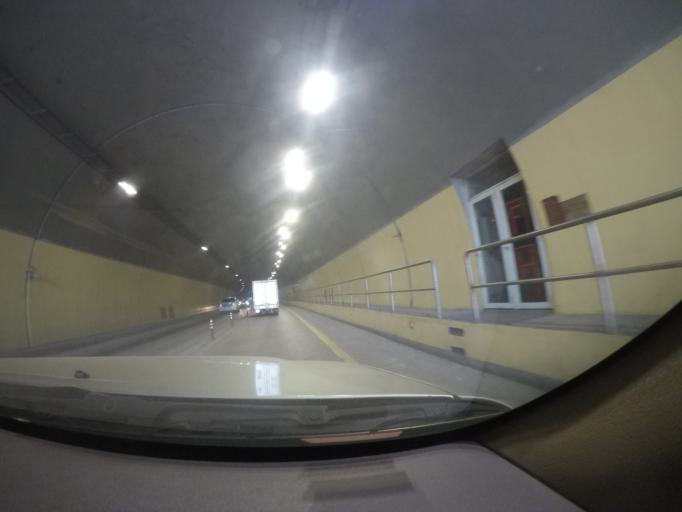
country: VN
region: Thua Thien-Hue
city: Phu Loc
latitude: 16.2646
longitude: 108.0326
